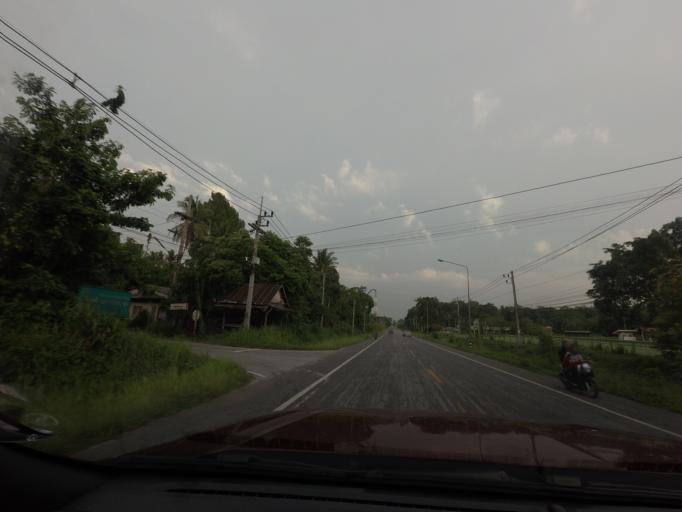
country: TH
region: Pattani
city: Mae Lan
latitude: 6.5930
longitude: 101.1955
